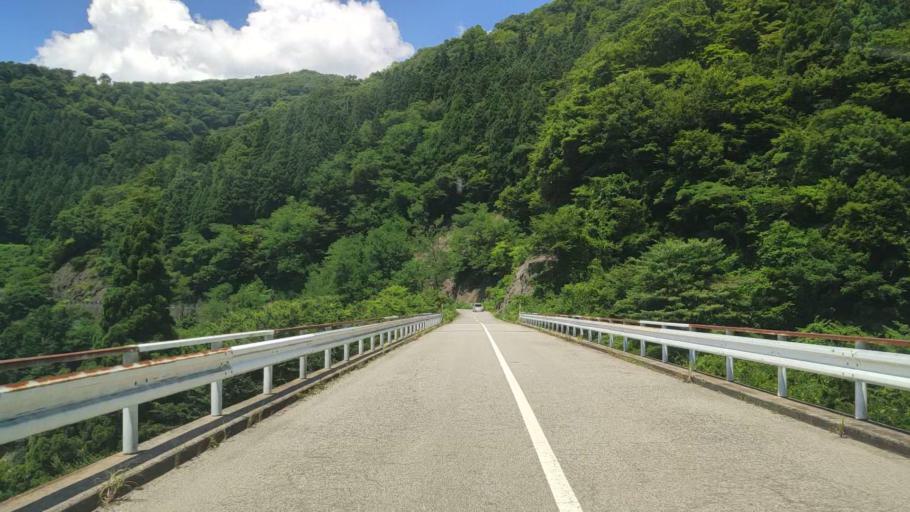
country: JP
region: Fukui
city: Ono
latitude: 35.9010
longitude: 136.5170
